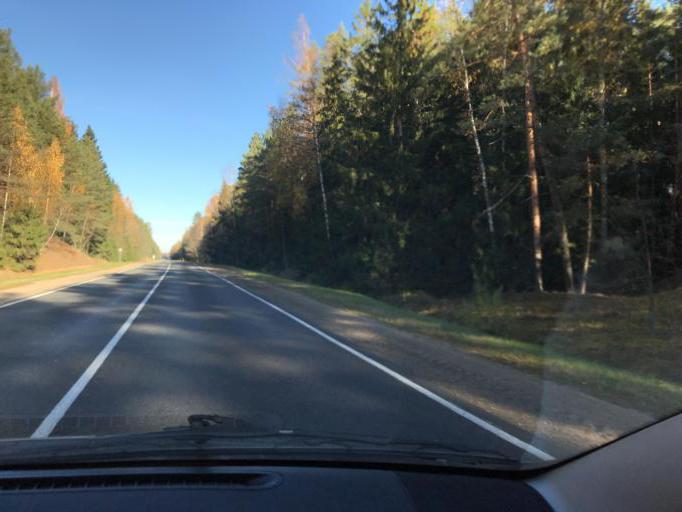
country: BY
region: Vitebsk
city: Polatsk
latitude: 55.3613
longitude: 28.8071
